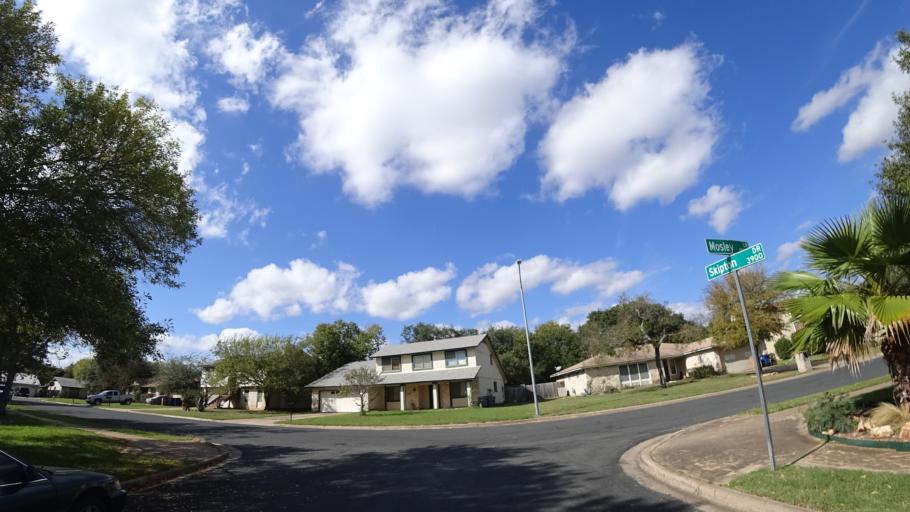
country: US
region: Texas
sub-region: Travis County
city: Wells Branch
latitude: 30.4165
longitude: -97.7223
